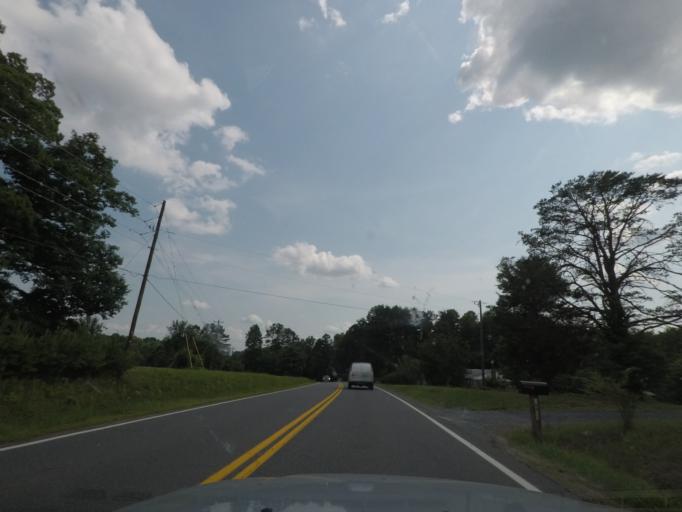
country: US
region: Virginia
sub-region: Fluvanna County
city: Palmyra
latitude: 37.9081
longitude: -78.2571
